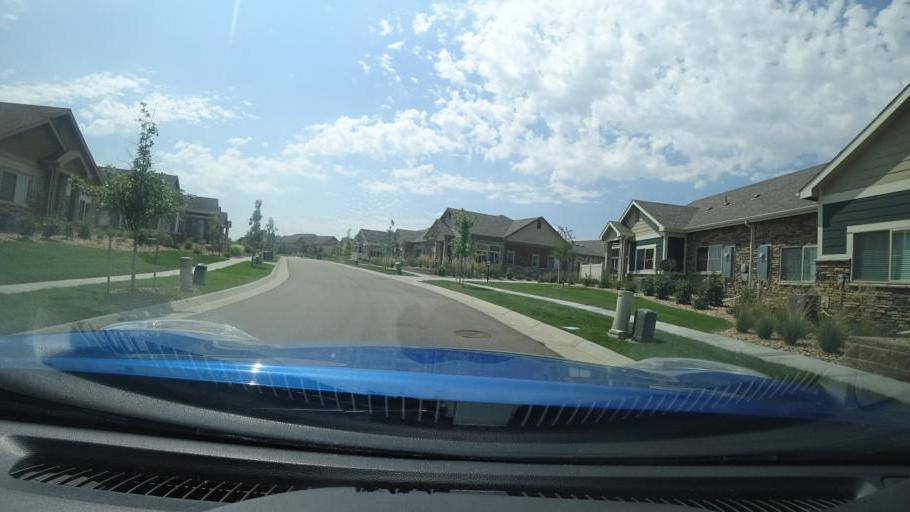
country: US
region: Colorado
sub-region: Adams County
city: Aurora
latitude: 39.6806
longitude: -104.7594
